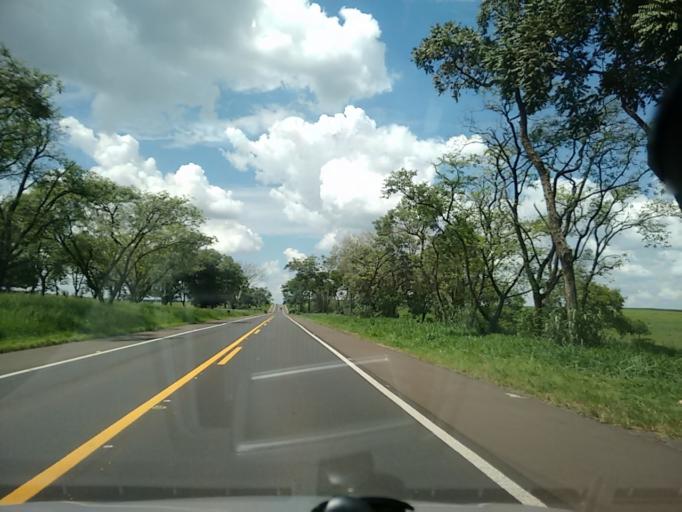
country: BR
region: Sao Paulo
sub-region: Osvaldo Cruz
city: Osvaldo Cruz
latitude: -21.8762
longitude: -50.8601
